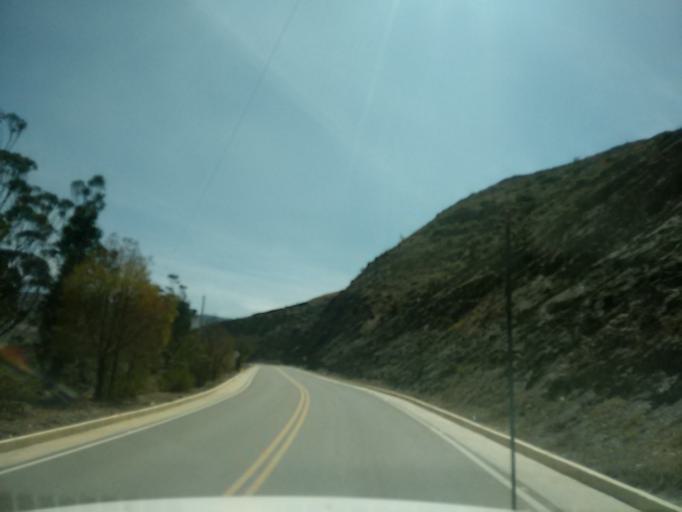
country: CO
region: Boyaca
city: Sachica
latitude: 5.5881
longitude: -73.5173
